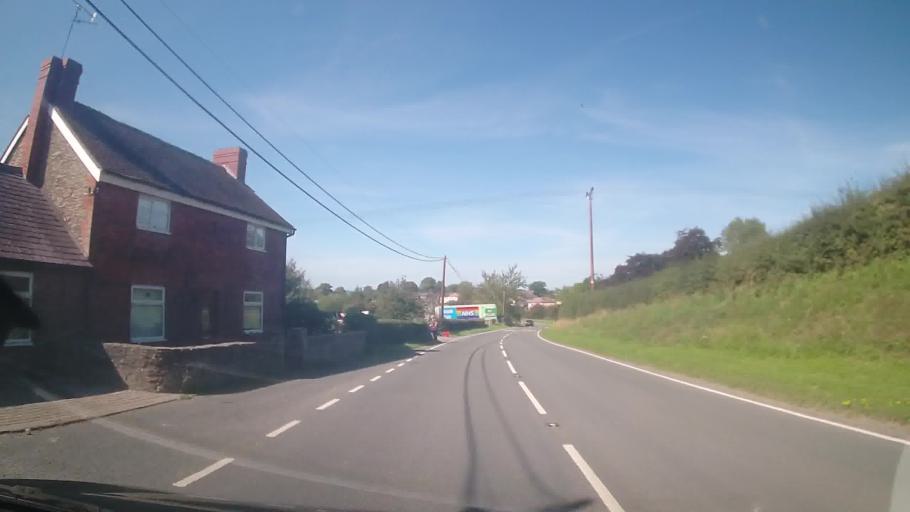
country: GB
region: England
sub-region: Shropshire
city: Mainstone
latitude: 52.5353
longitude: -3.0598
